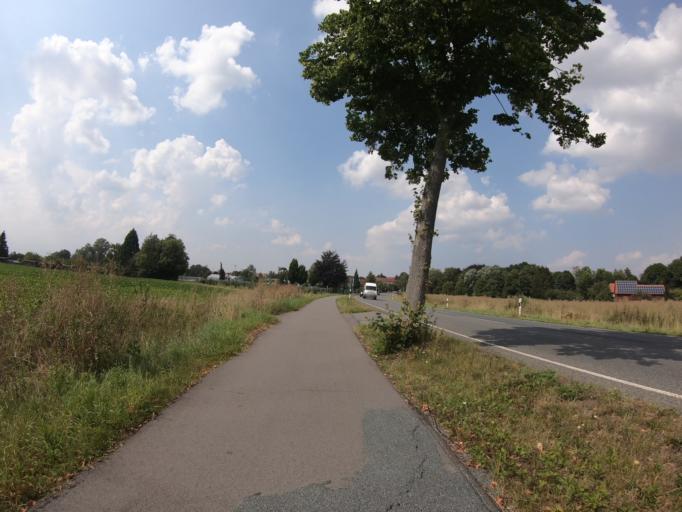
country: DE
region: Lower Saxony
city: Sickte
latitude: 52.2150
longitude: 10.6481
